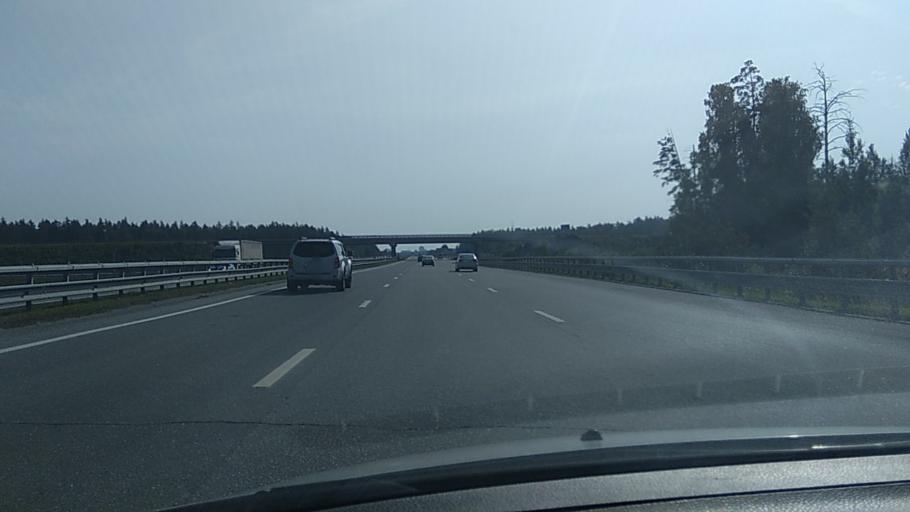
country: RU
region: Sverdlovsk
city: Shuvakish
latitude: 56.9383
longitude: 60.5116
